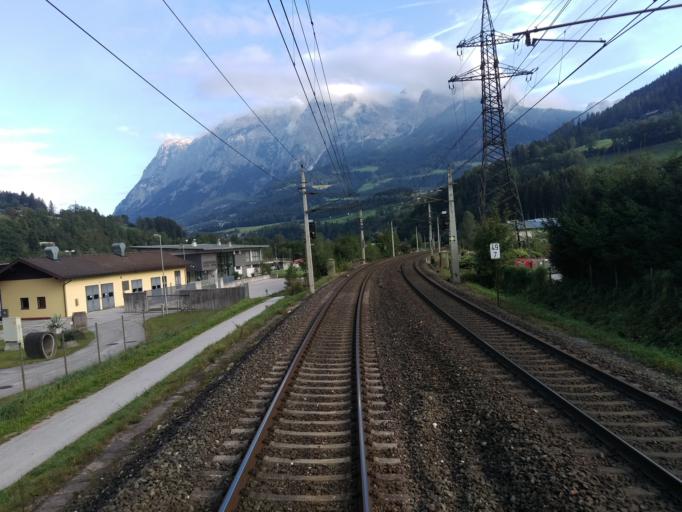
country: AT
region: Salzburg
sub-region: Politischer Bezirk Sankt Johann im Pongau
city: Pfarrwerfen
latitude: 47.4378
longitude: 13.2116
